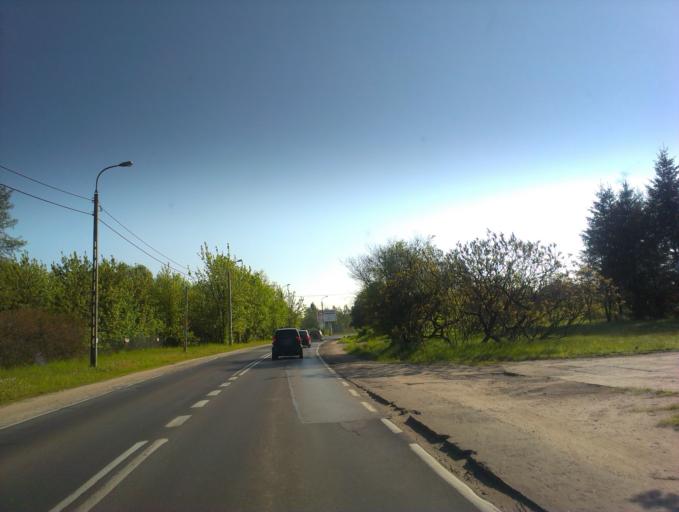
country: PL
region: Masovian Voivodeship
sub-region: Powiat piaseczynski
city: Konstancin-Jeziorna
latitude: 52.0883
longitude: 21.1039
